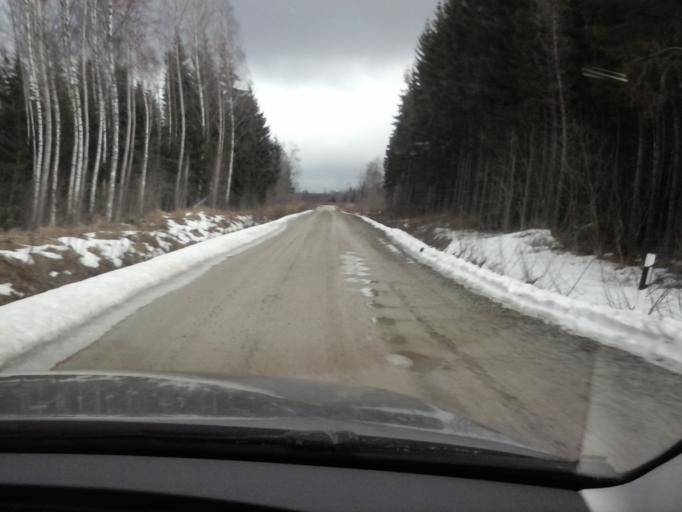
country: EE
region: Jogevamaa
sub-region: Mustvee linn
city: Mustvee
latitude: 59.0719
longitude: 26.8696
